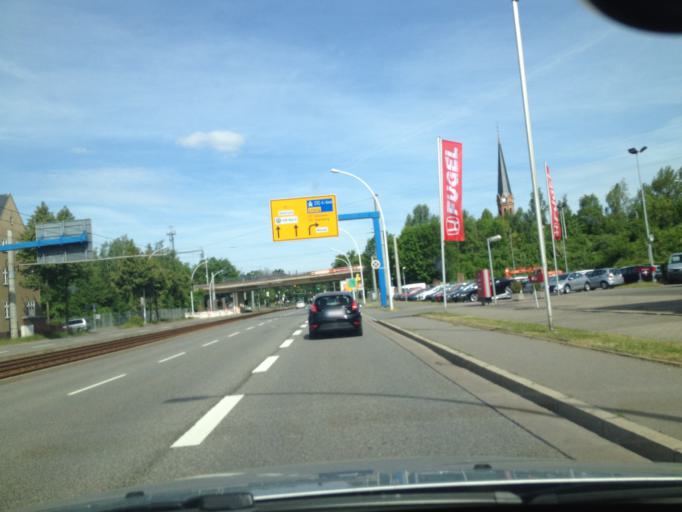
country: DE
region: Saxony
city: Chemnitz
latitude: 50.7974
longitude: 12.9163
